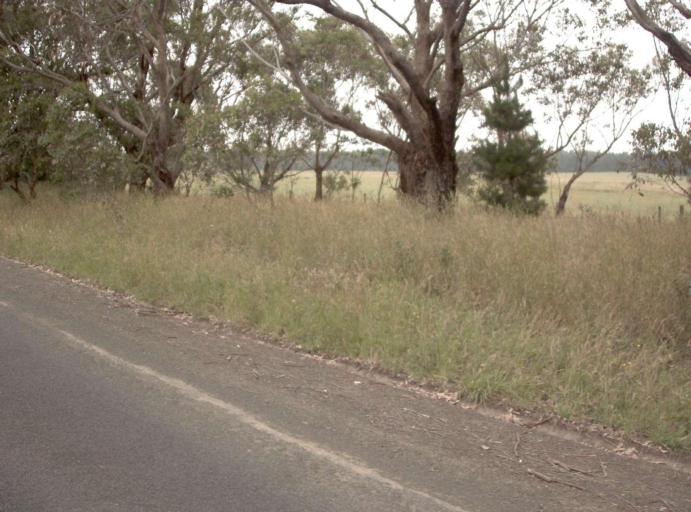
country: AU
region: Victoria
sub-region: Latrobe
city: Morwell
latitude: -38.2846
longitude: 146.3696
